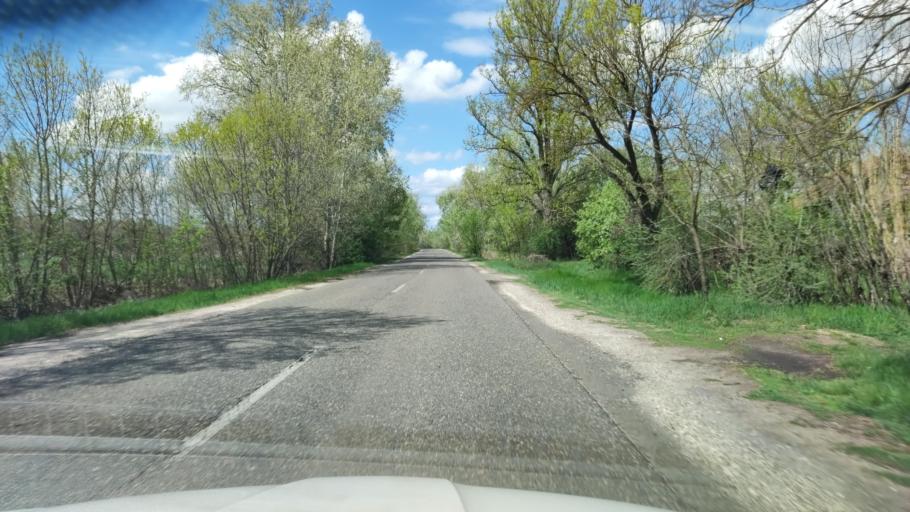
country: HU
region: Pest
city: Tortel
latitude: 47.1347
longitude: 19.9014
